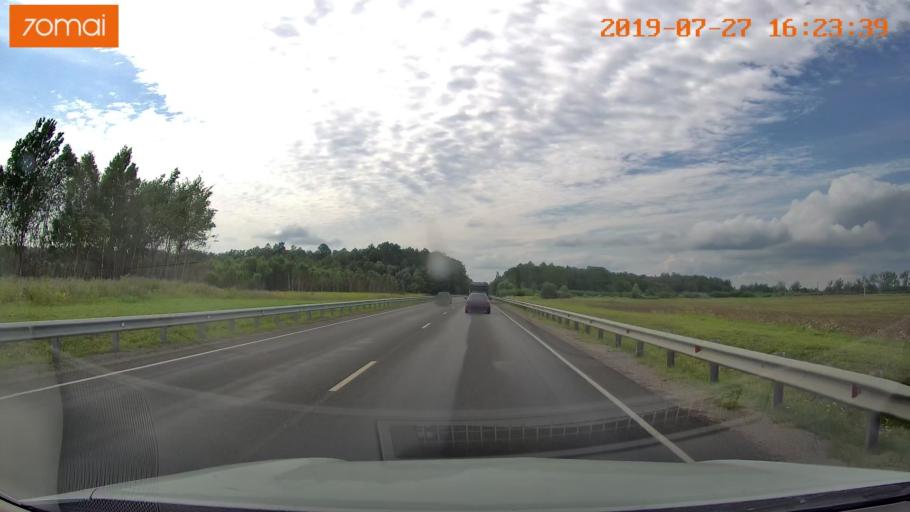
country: RU
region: Kaliningrad
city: Zheleznodorozhnyy
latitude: 54.6316
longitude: 21.4691
